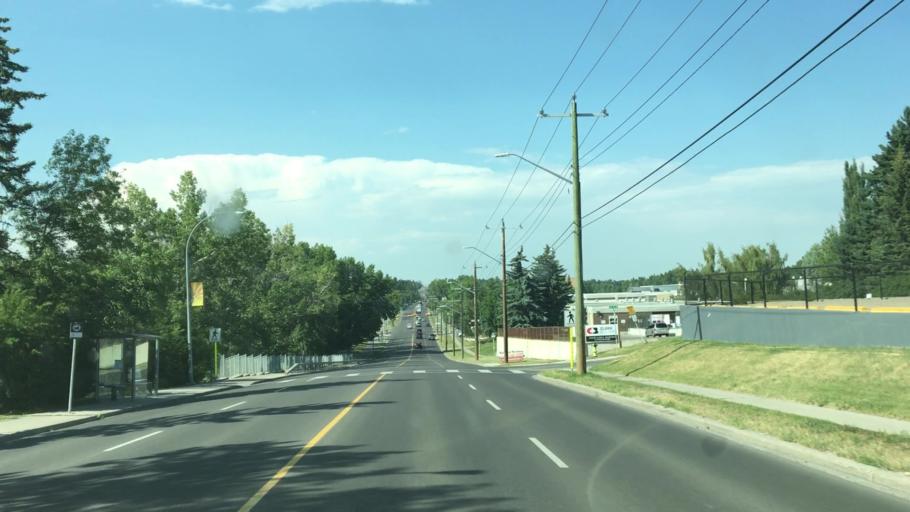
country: CA
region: Alberta
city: Calgary
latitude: 51.0846
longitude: -114.0716
